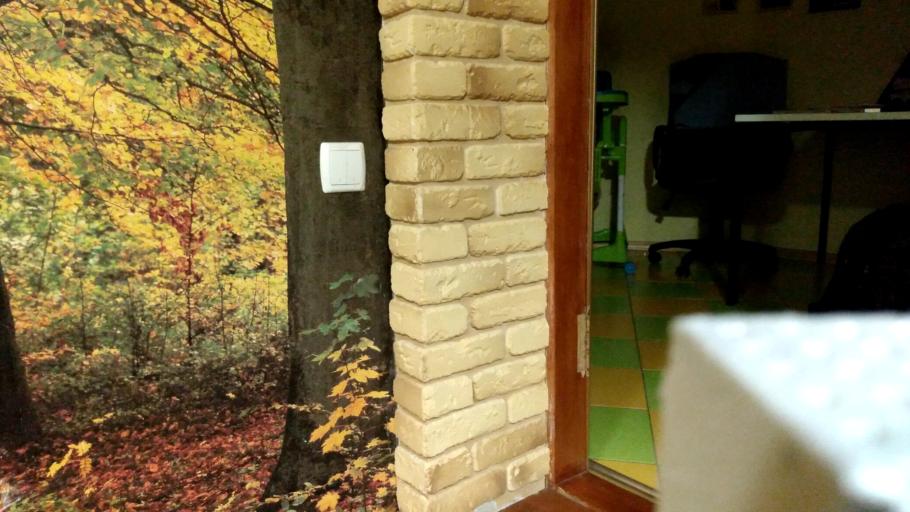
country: RU
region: Arkhangelskaya
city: Kargopol'
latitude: 61.4567
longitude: 37.7958
